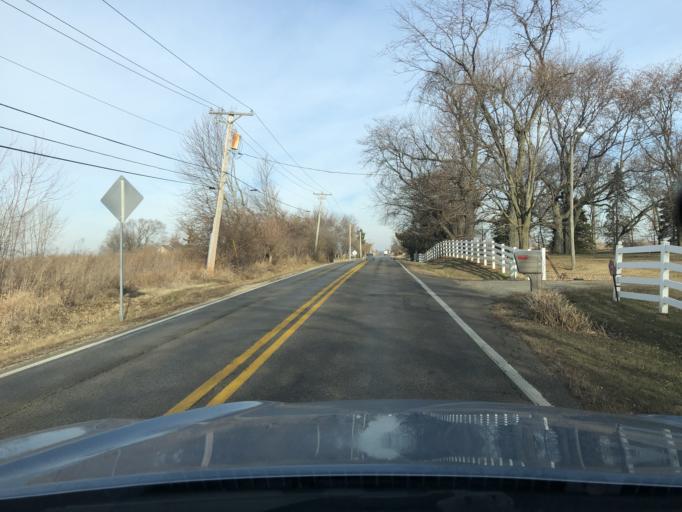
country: US
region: Illinois
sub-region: McHenry County
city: Lake in the Hills
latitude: 42.1421
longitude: -88.3456
